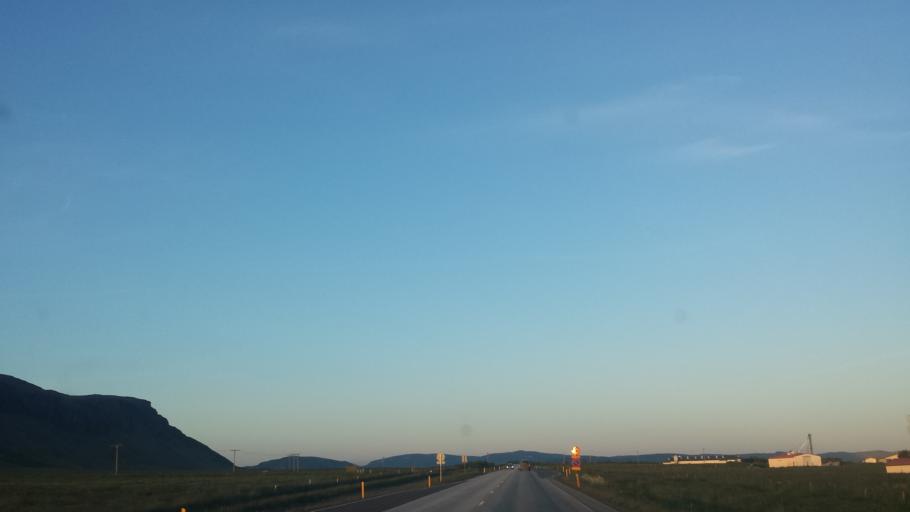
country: IS
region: Capital Region
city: Mosfellsbaer
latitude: 64.2154
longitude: -21.7836
